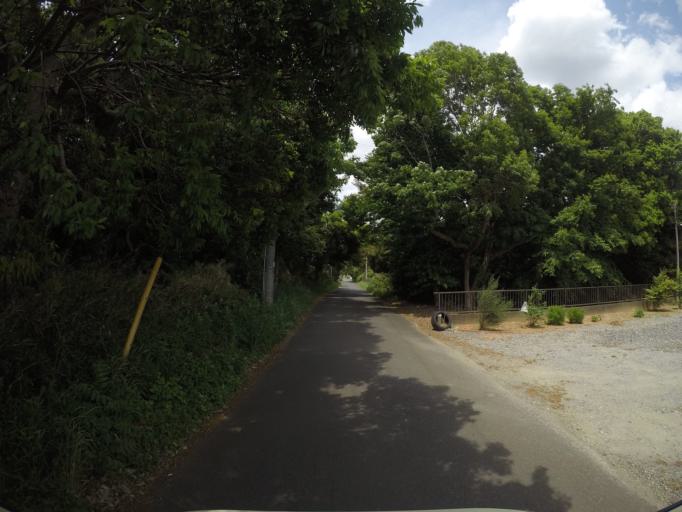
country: JP
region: Ibaraki
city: Ushiku
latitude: 35.9710
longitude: 140.1172
